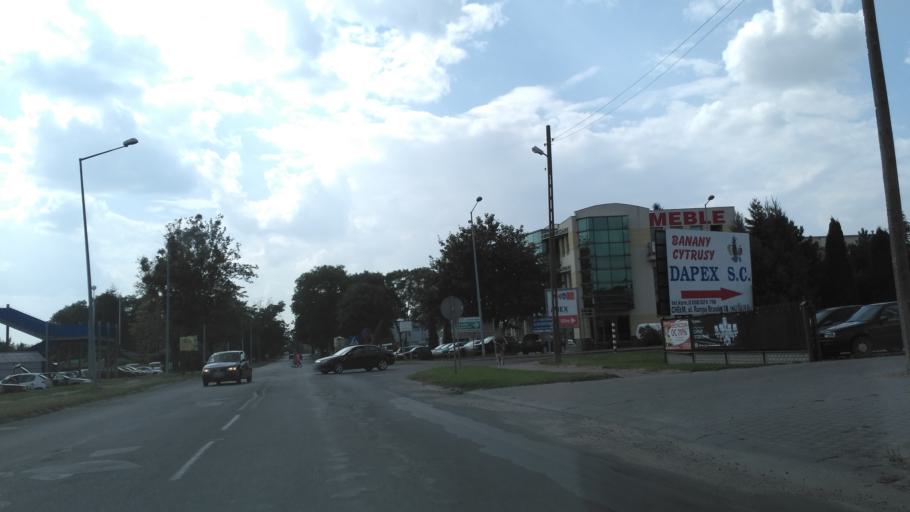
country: PL
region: Lublin Voivodeship
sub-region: Chelm
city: Chelm
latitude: 51.1425
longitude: 23.4941
